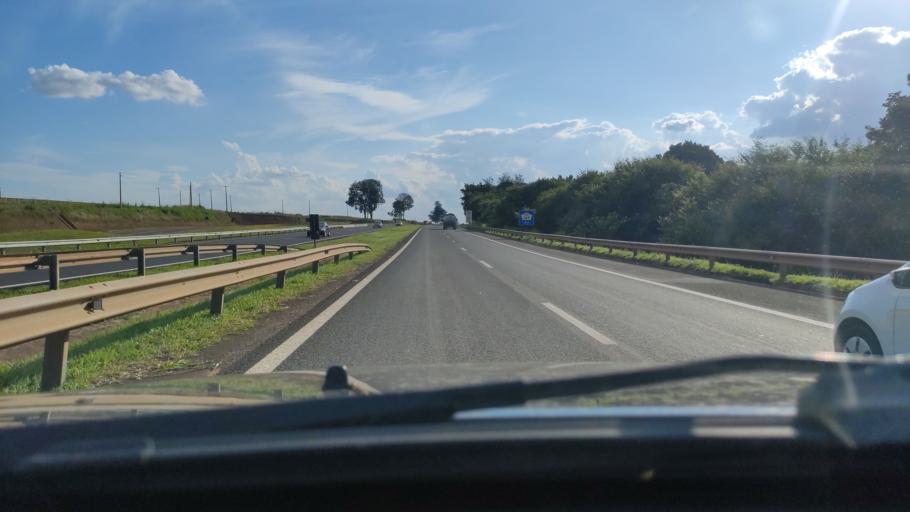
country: BR
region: Sao Paulo
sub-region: Itapira
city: Itapira
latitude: -22.4522
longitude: -46.8546
